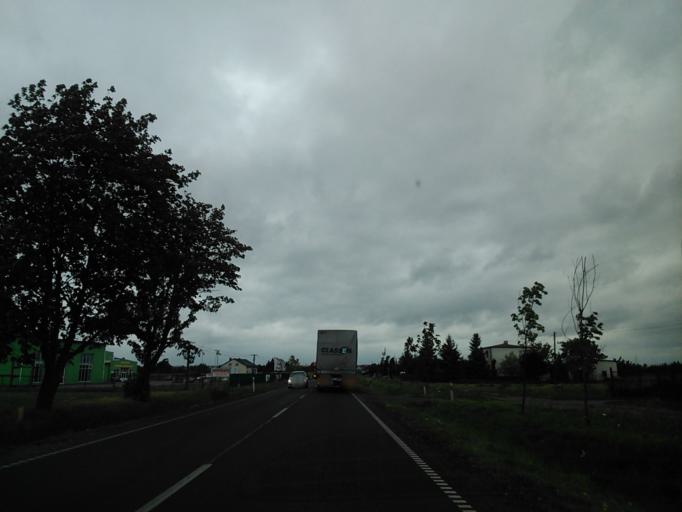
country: PL
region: Kujawsko-Pomorskie
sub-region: Powiat inowroclawski
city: Kruszwica
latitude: 52.6688
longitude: 18.3451
